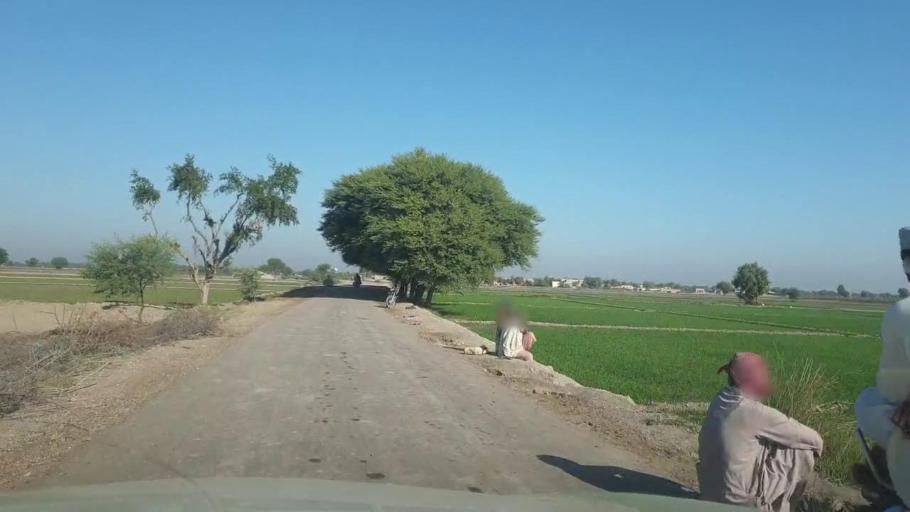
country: PK
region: Sindh
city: Bhan
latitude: 26.5305
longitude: 67.6748
